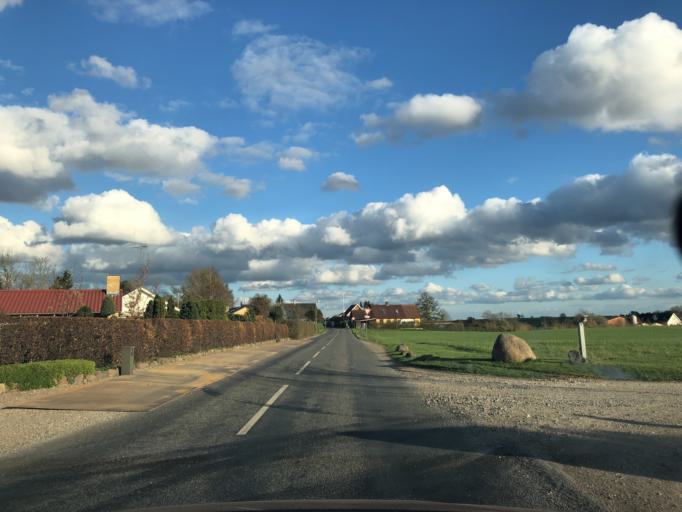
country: DK
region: Zealand
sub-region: Ringsted Kommune
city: Ringsted
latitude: 55.4956
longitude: 11.8633
